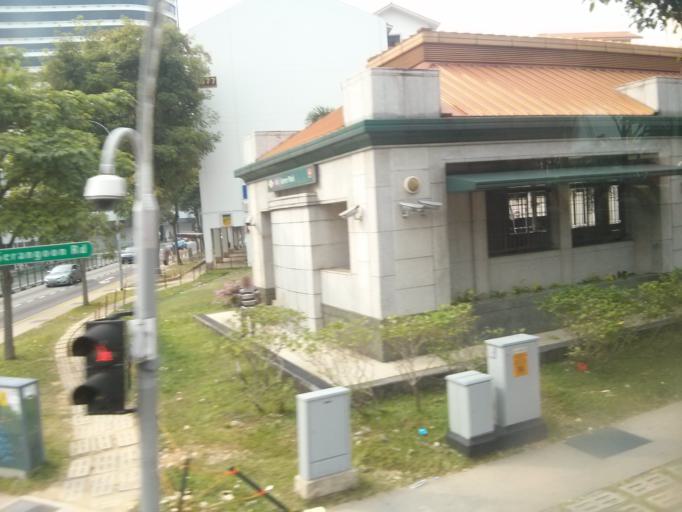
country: SG
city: Singapore
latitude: 1.3119
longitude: 103.8554
